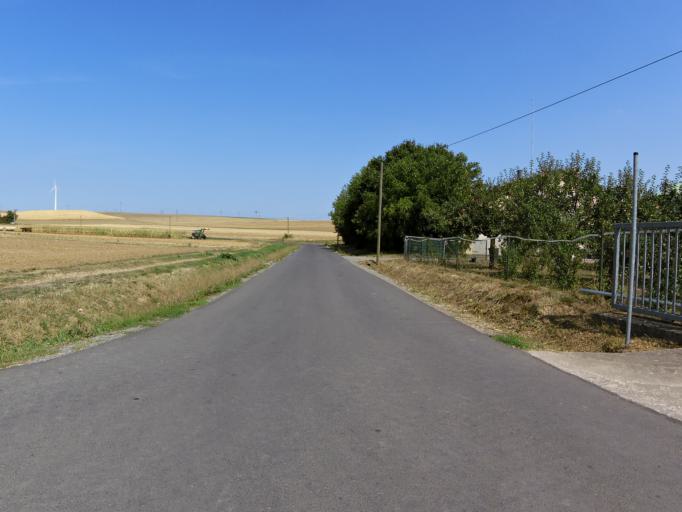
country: DE
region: Bavaria
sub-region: Regierungsbezirk Unterfranken
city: Theilheim
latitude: 49.7609
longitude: 10.0375
